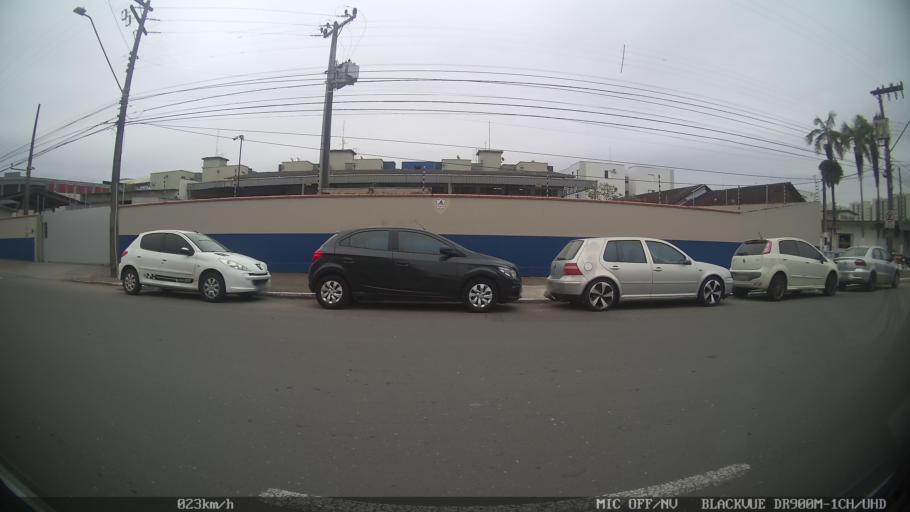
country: BR
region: Santa Catarina
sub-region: Joinville
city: Joinville
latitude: -26.3149
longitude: -48.8328
